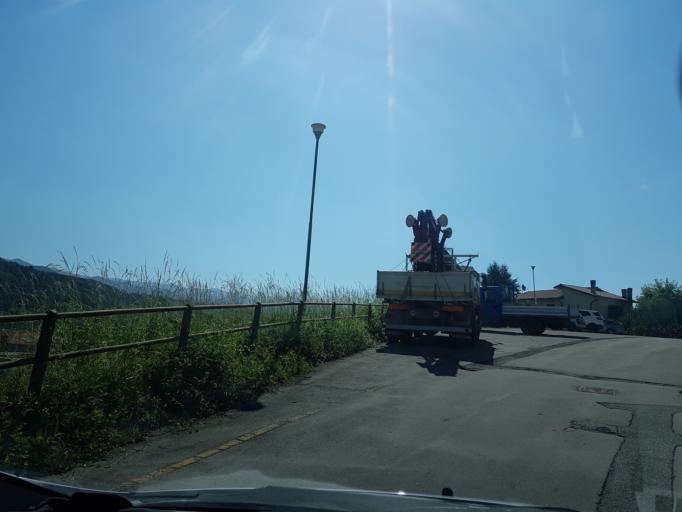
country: IT
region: Tuscany
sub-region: Provincia di Lucca
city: Camporgiano
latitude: 44.1585
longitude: 10.3318
